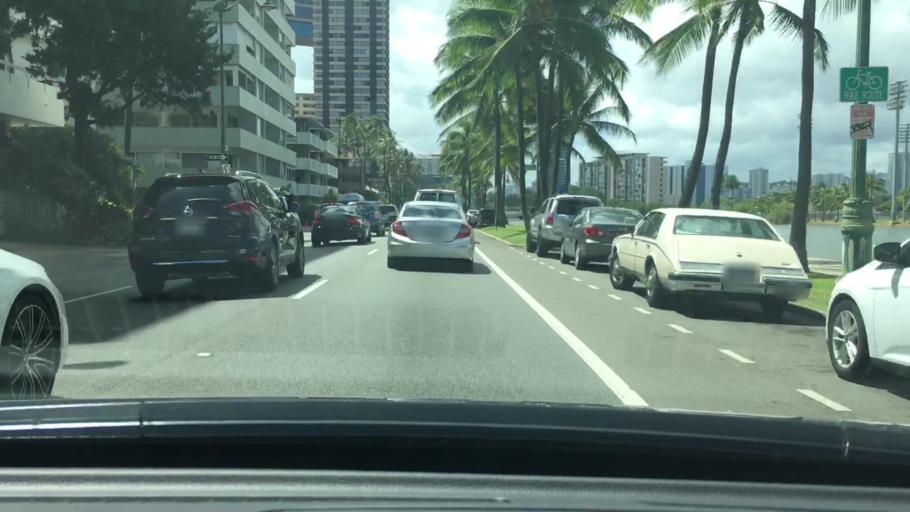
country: US
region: Hawaii
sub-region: Honolulu County
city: Honolulu
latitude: 21.2855
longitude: -157.8302
